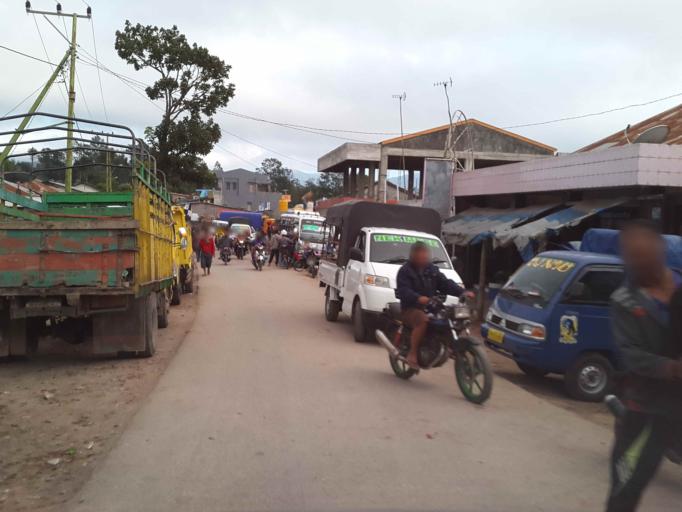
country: ID
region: East Nusa Tenggara
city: Kapan
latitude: -9.7317
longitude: 124.2726
